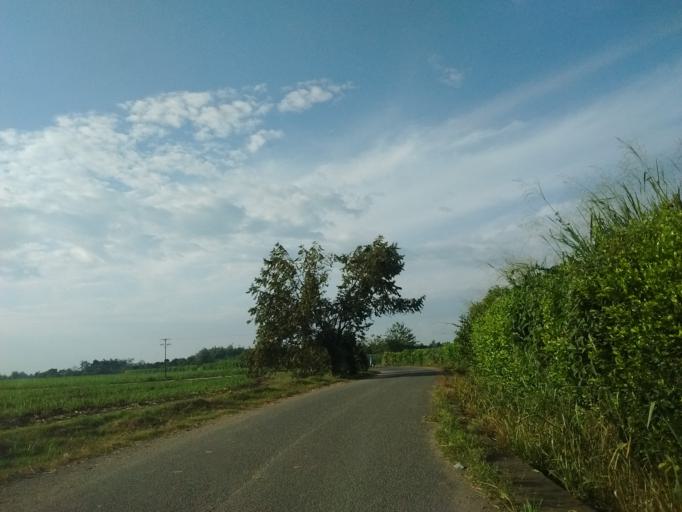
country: CO
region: Cauca
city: Puerto Tejada
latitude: 3.2092
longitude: -76.4441
